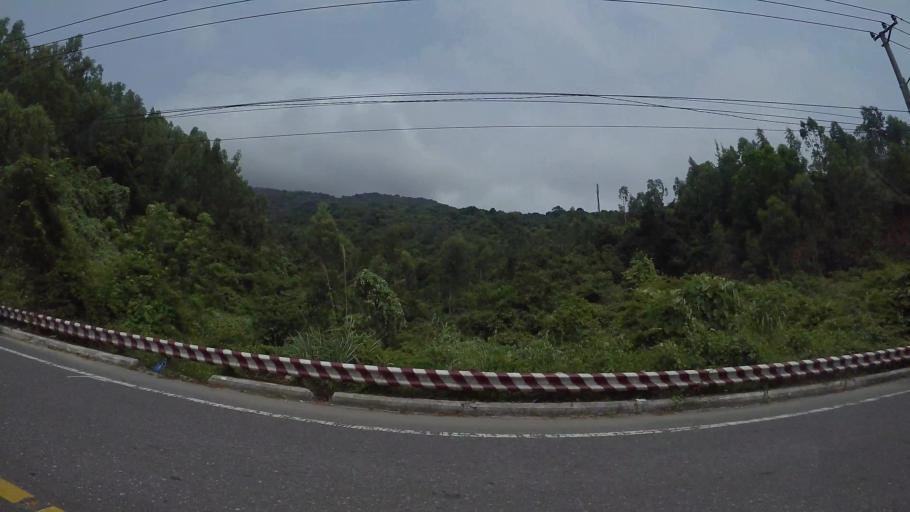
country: VN
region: Da Nang
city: Son Tra
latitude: 16.1007
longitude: 108.2714
